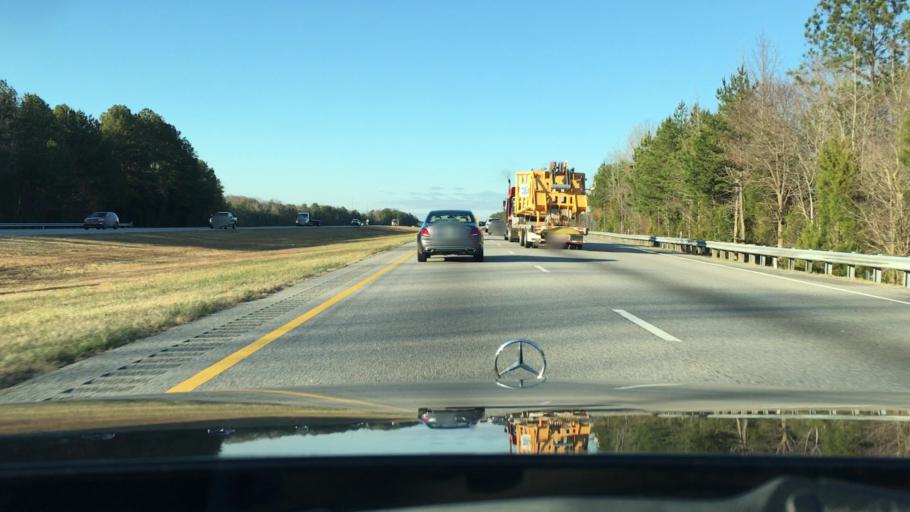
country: US
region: South Carolina
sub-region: Chester County
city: Eureka Mill
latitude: 34.7081
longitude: -81.0304
